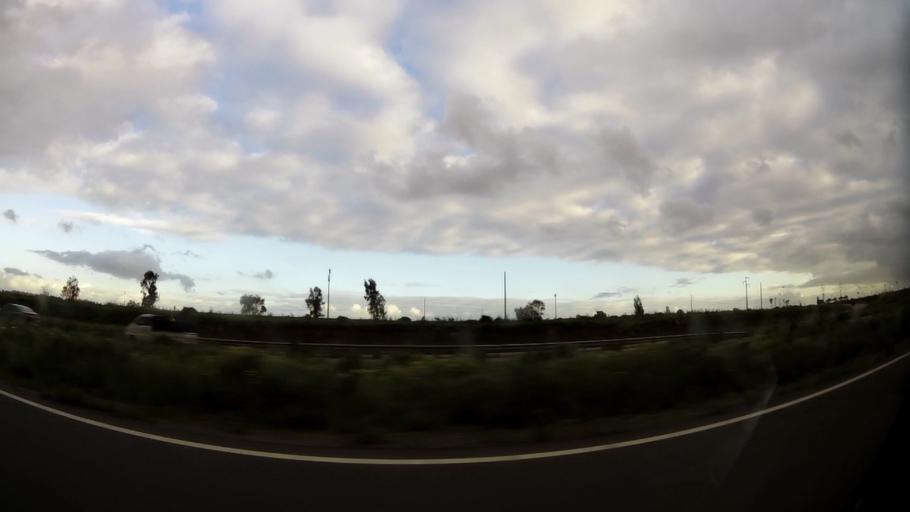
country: MA
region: Grand Casablanca
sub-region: Mediouna
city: Tit Mellil
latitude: 33.5646
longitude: -7.4924
